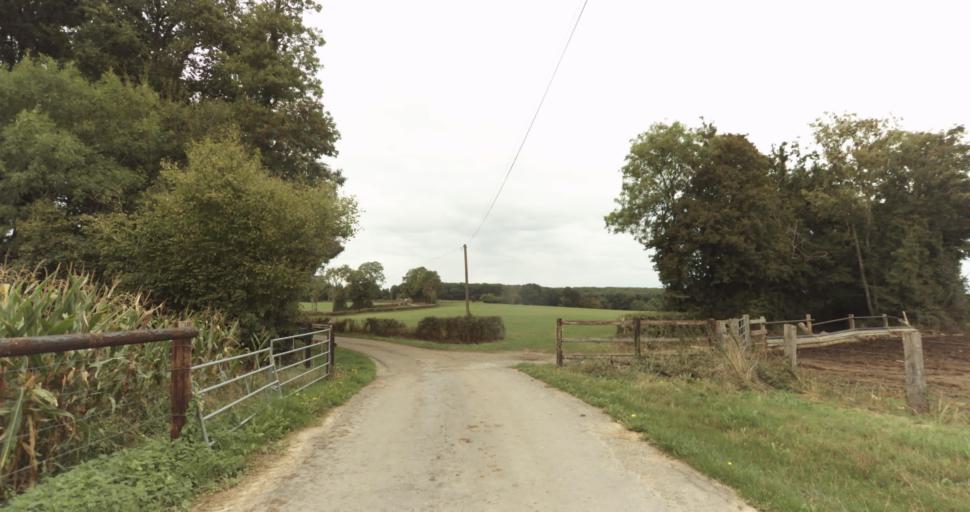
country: FR
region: Lower Normandy
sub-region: Departement de l'Orne
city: Sees
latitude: 48.6751
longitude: 0.2695
